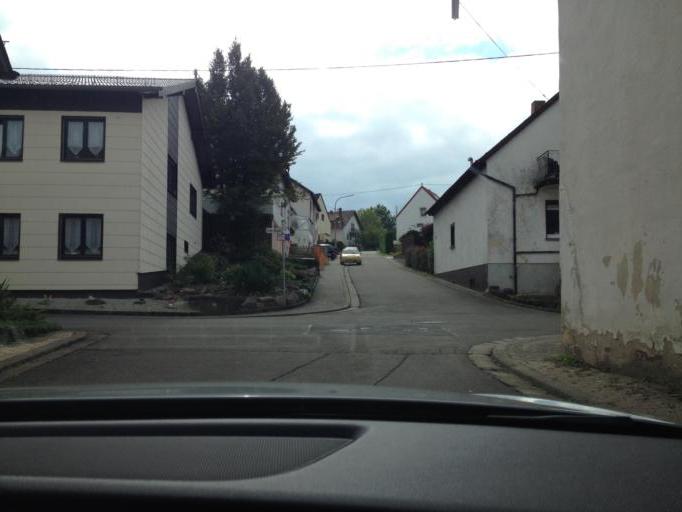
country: DE
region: Rheinland-Pfalz
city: Gimbweiler
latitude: 49.5651
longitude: 7.1797
